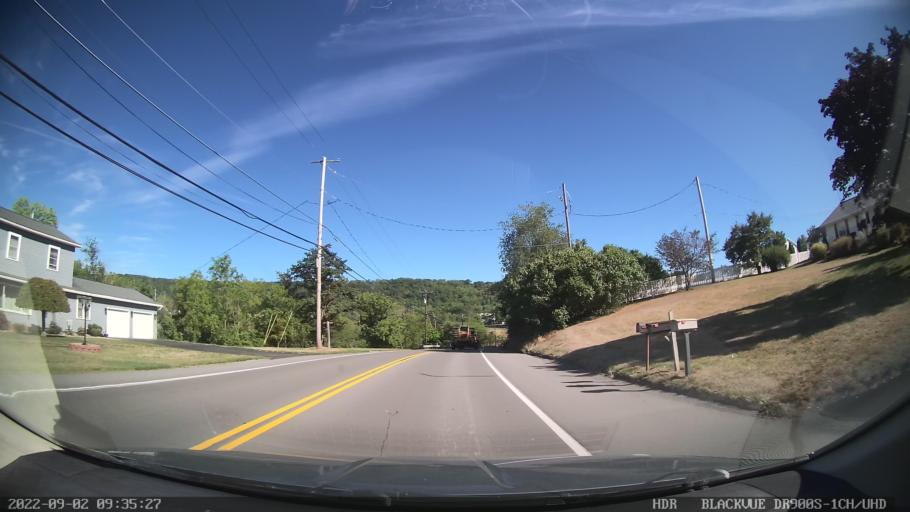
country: US
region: Pennsylvania
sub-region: Northumberland County
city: Elysburg
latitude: 40.8721
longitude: -76.5556
